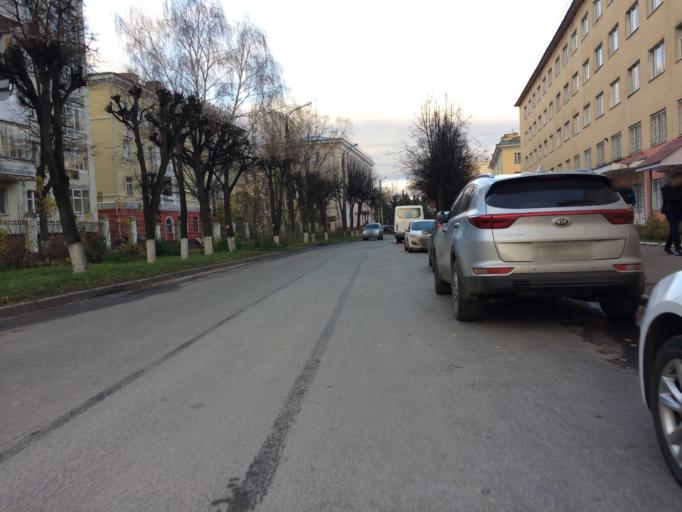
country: RU
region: Mariy-El
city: Yoshkar-Ola
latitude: 56.6289
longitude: 47.8907
